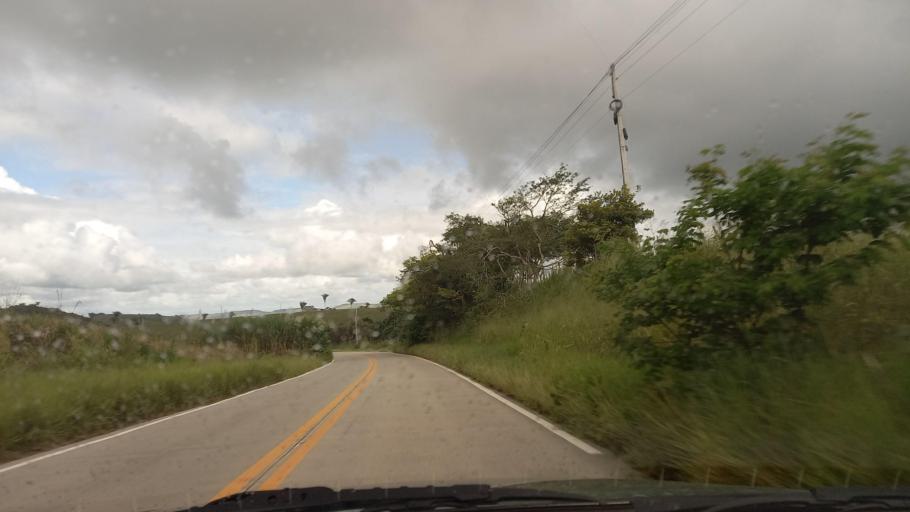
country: BR
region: Pernambuco
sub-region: Quipapa
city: Quipapa
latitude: -8.7904
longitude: -35.9886
